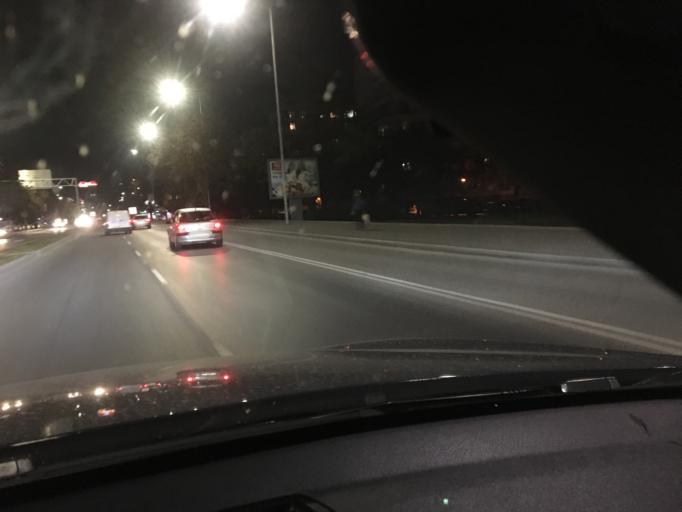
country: BG
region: Varna
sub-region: Obshtina Varna
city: Varna
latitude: 43.2147
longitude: 27.8984
